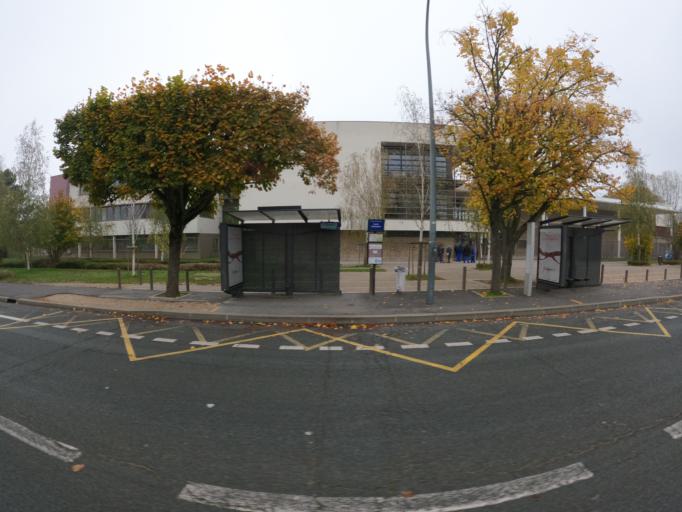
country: FR
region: Ile-de-France
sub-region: Departement du Val-de-Marne
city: Chennevieres-sur-Marne
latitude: 48.7985
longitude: 2.5558
